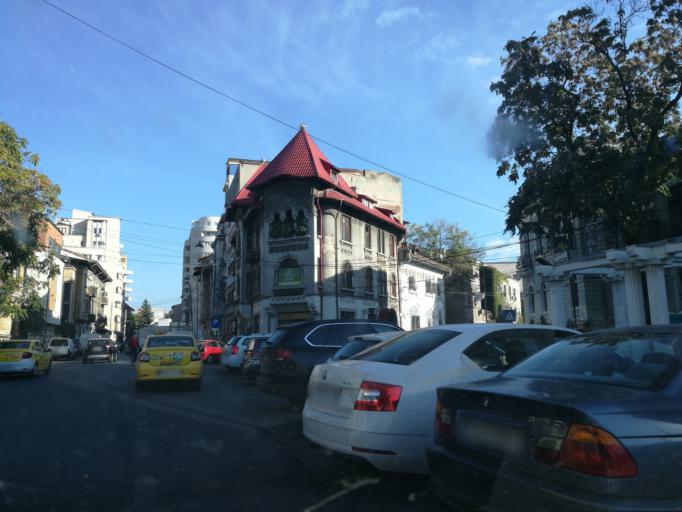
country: RO
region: Bucuresti
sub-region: Municipiul Bucuresti
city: Bucharest
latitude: 44.4423
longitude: 26.1097
